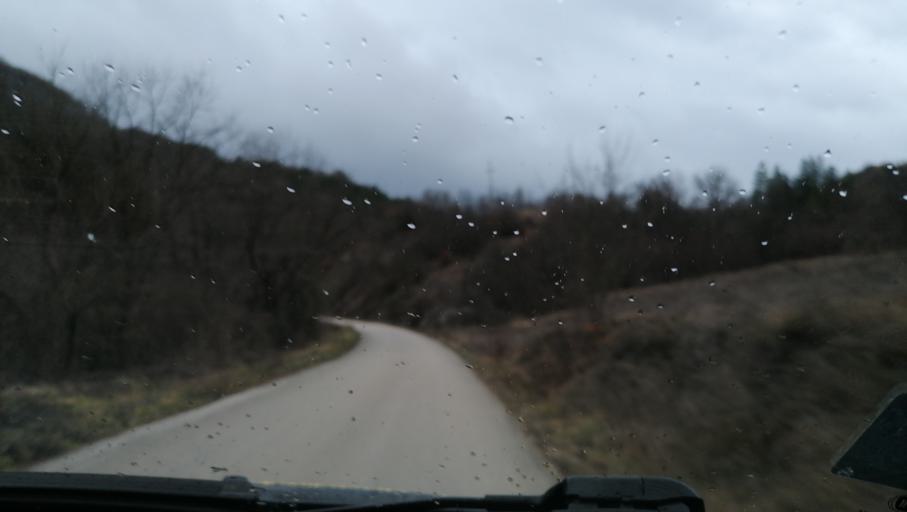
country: RS
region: Central Serbia
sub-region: Pirotski Okrug
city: Dimitrovgrad
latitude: 42.9780
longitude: 22.6528
